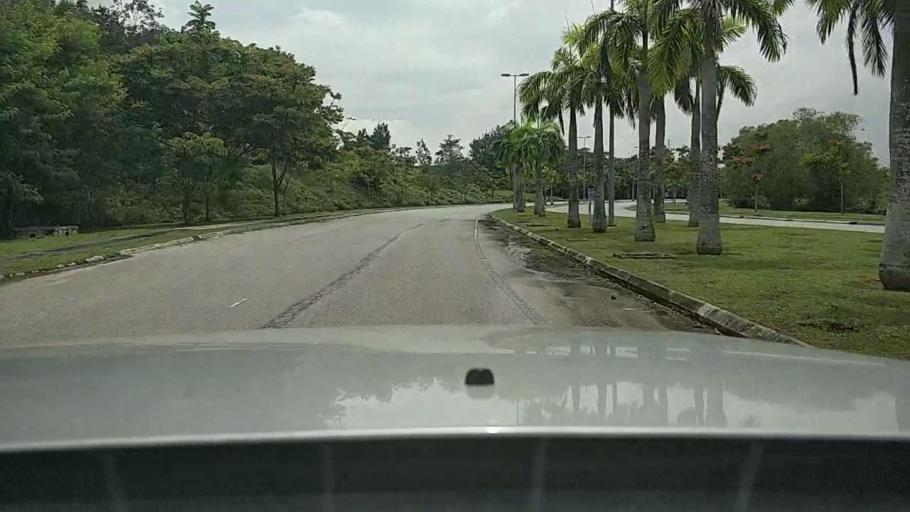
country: MY
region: Putrajaya
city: Putrajaya
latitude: 2.9039
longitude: 101.6525
